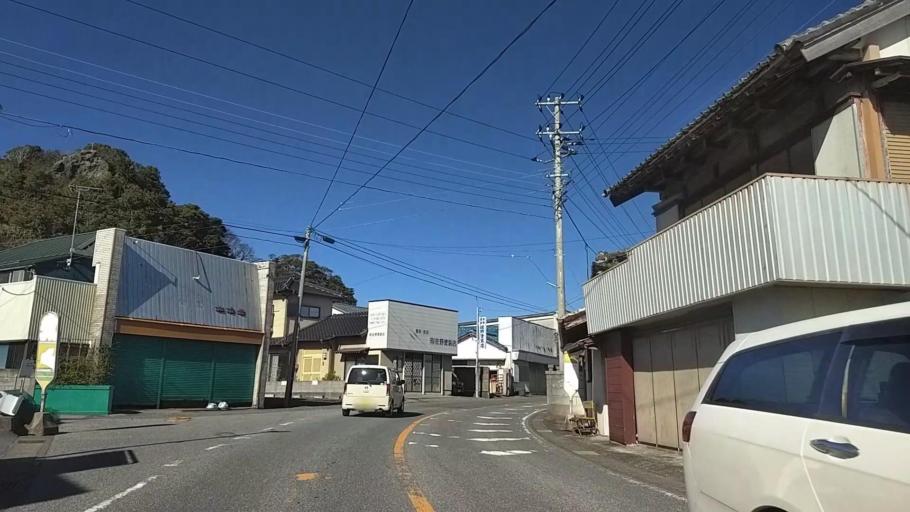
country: JP
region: Chiba
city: Tateyama
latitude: 34.9570
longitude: 139.9594
